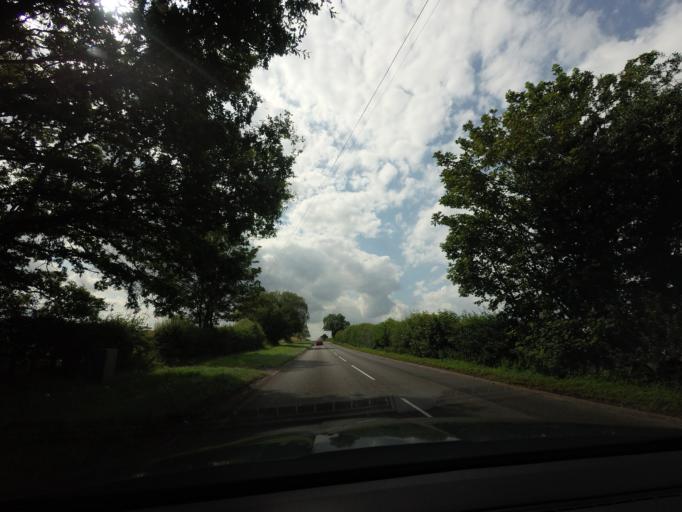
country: GB
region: England
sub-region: Staffordshire
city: Brewood
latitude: 52.6938
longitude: -2.1401
